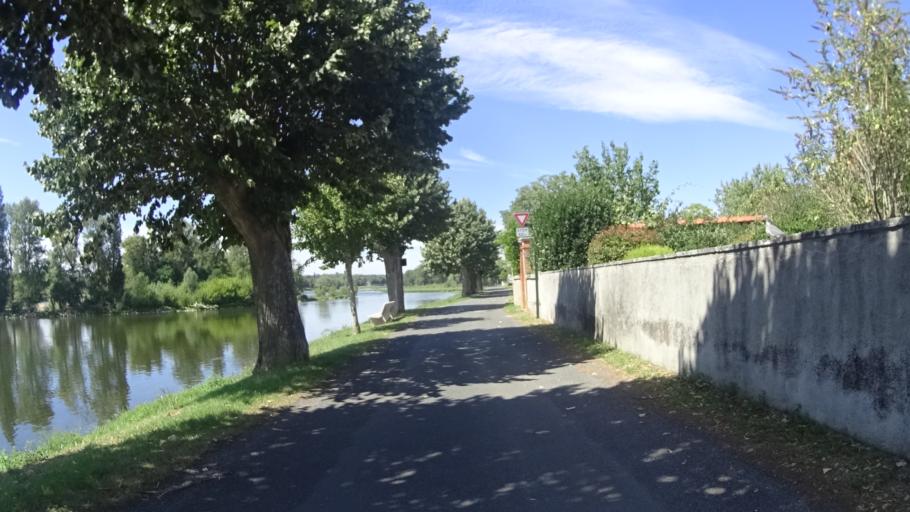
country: FR
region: Centre
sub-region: Departement du Loiret
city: Bonny-sur-Loire
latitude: 47.5882
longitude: 2.7850
